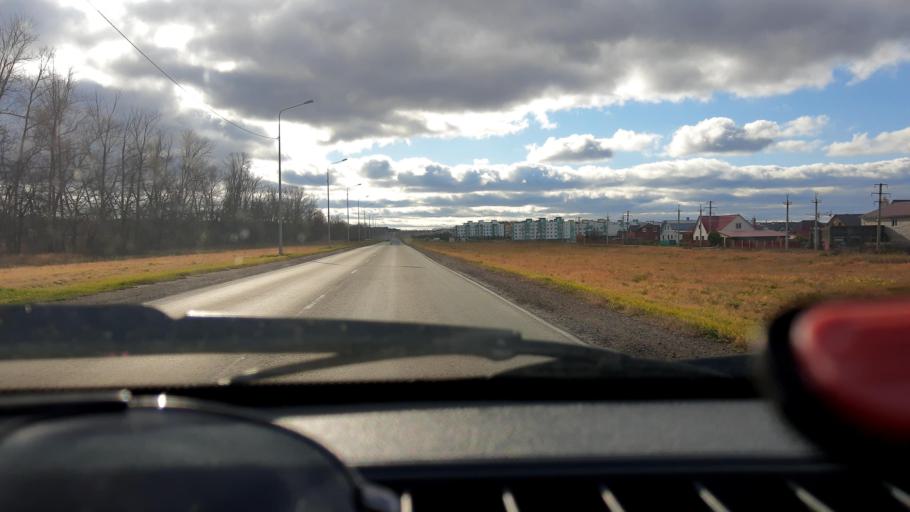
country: RU
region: Bashkortostan
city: Avdon
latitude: 54.4878
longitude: 55.8958
